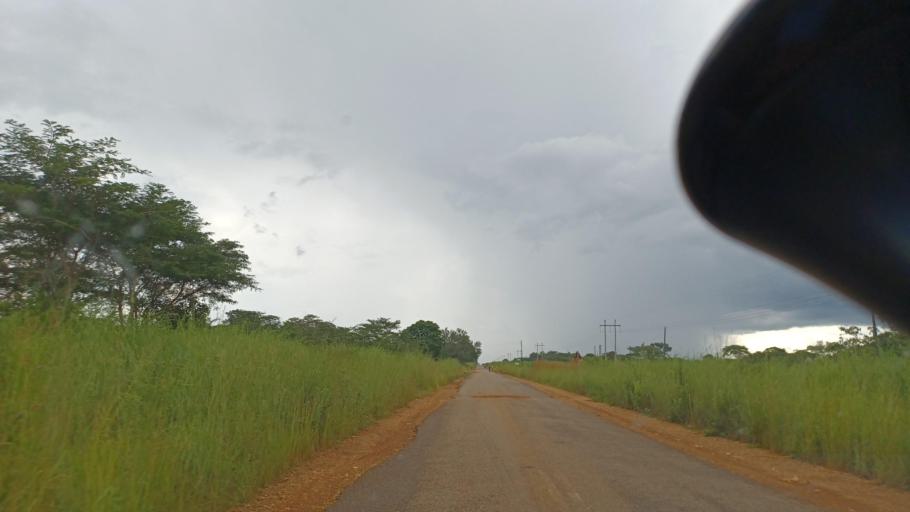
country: ZM
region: North-Western
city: Kasempa
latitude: -13.0152
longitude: 26.0024
